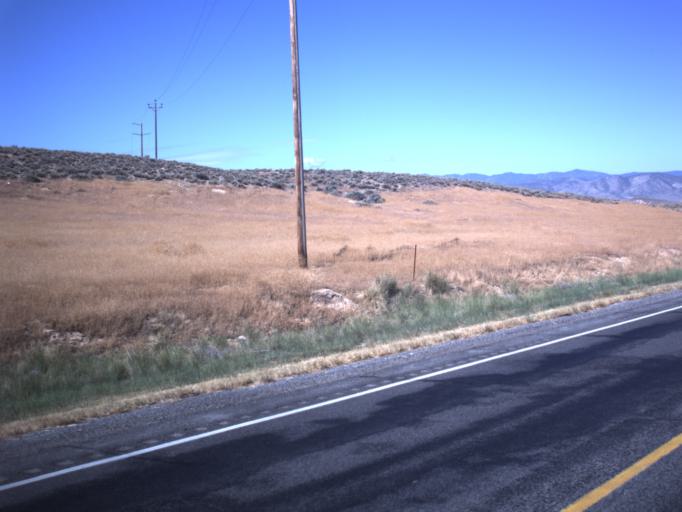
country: US
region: Utah
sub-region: Sanpete County
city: Gunnison
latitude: 39.1607
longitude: -111.7870
